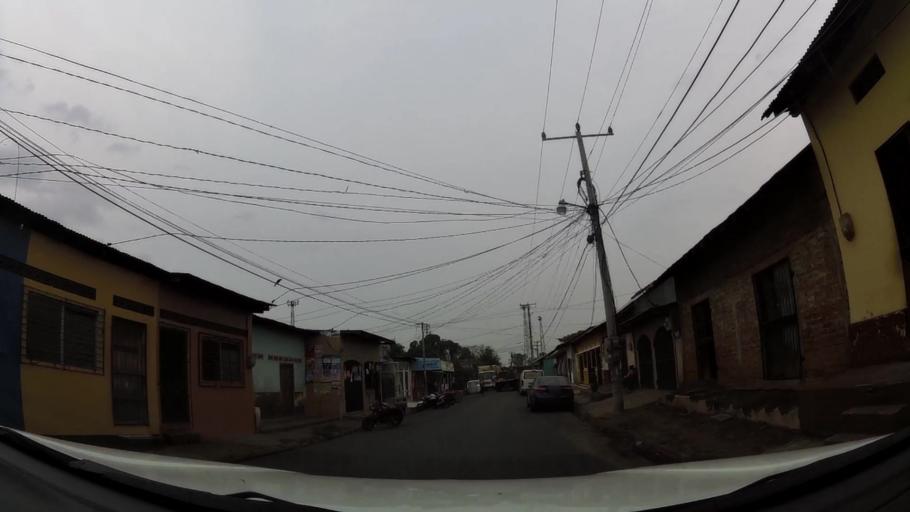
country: NI
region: Leon
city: Leon
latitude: 12.4466
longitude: -86.8792
